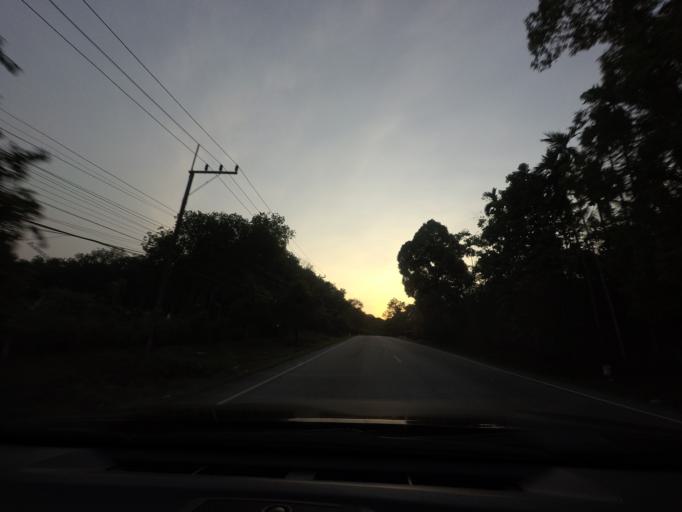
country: TH
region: Narathiwat
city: Rueso
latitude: 6.3641
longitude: 101.6047
